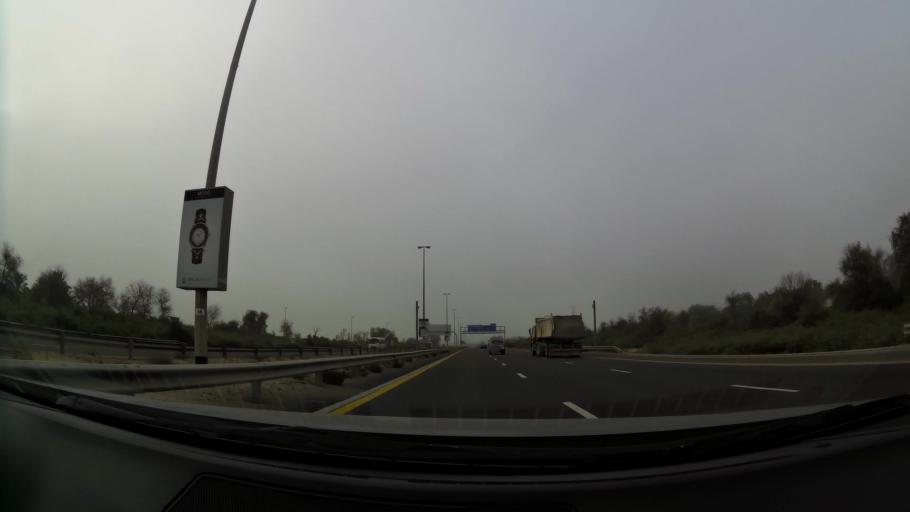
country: AE
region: Dubai
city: Dubai
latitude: 25.1595
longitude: 55.3327
